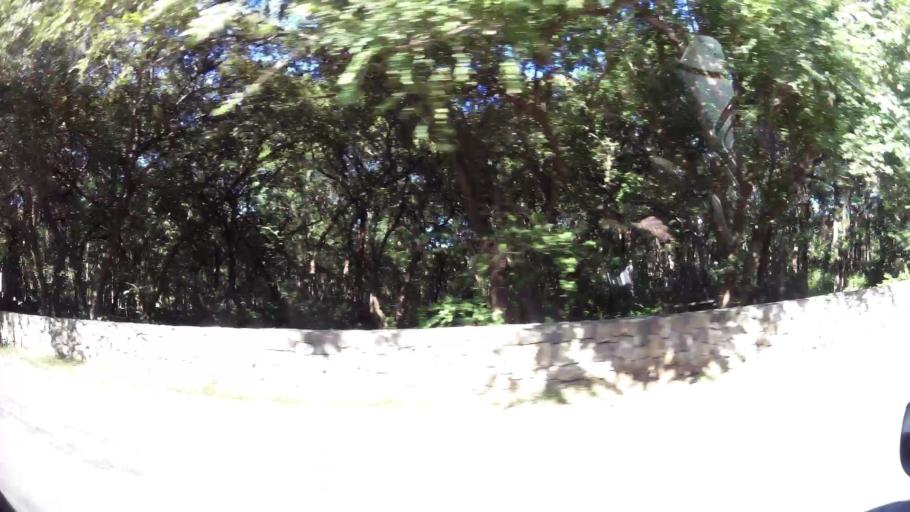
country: CR
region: Guanacaste
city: Sardinal
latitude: 10.5893
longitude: -85.6487
